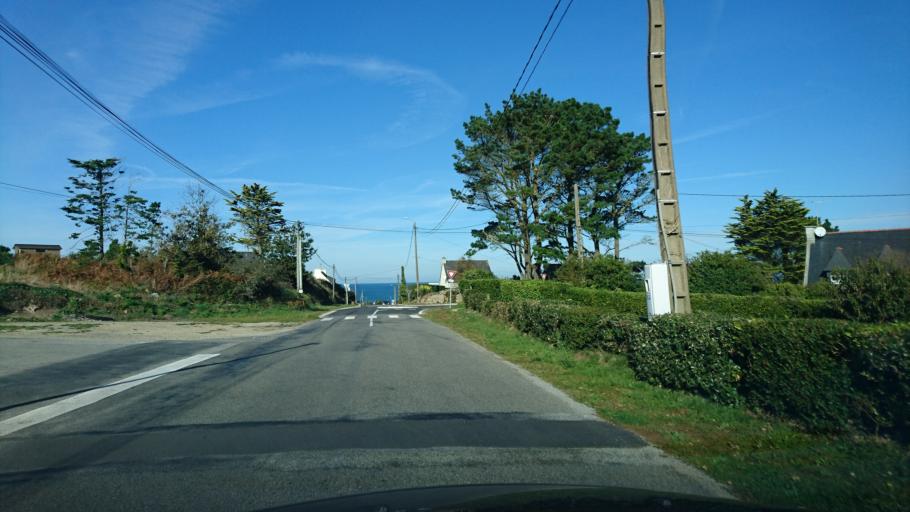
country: FR
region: Brittany
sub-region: Departement du Finistere
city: Lampaul-Plouarzel
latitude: 48.4339
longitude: -4.7718
